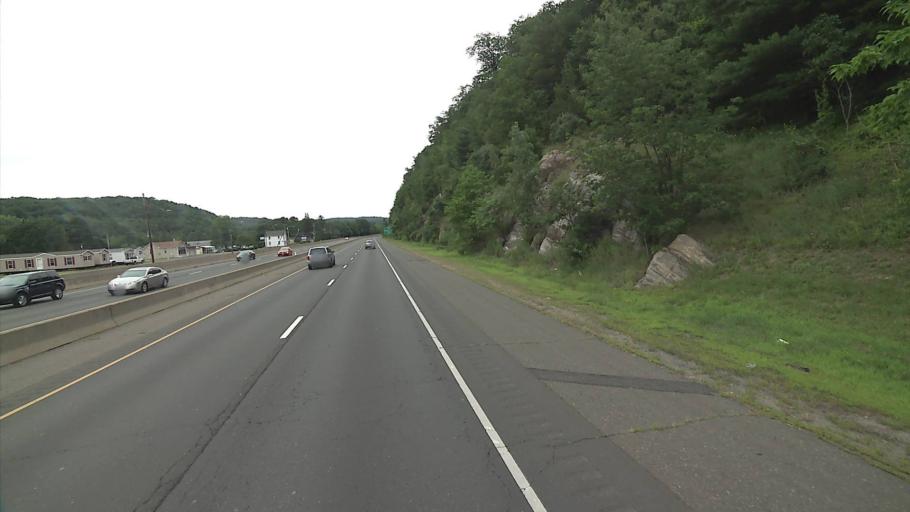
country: US
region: Connecticut
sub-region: New Haven County
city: Seymour
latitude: 41.4107
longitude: -73.0701
